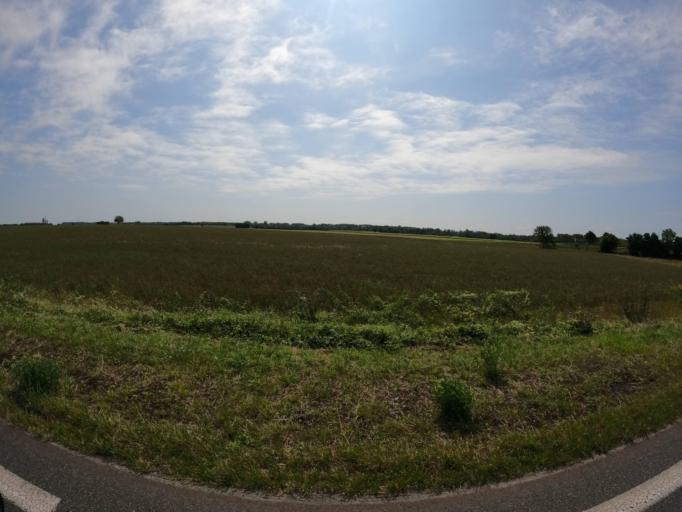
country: FR
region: Poitou-Charentes
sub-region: Departement des Deux-Sevres
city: Frontenay-Rohan-Rohan
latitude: 46.2442
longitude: -0.5701
